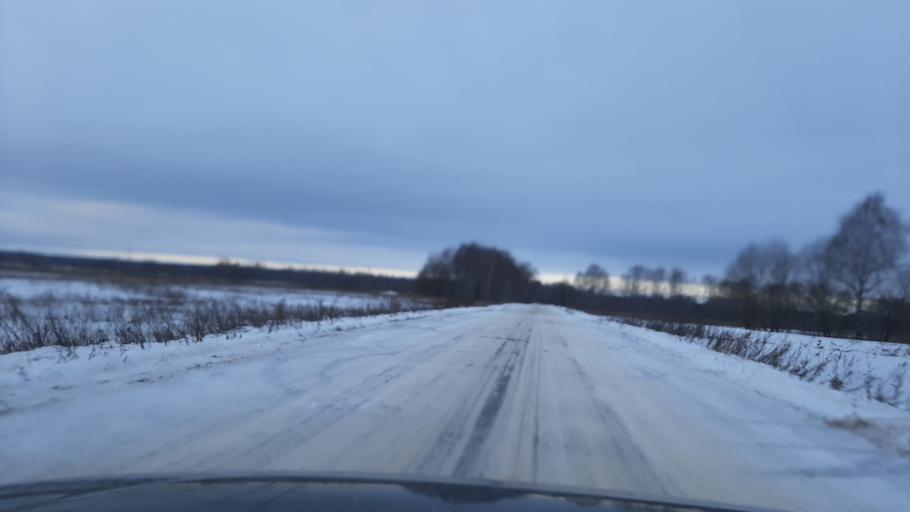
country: RU
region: Kostroma
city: Volgorechensk
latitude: 57.4367
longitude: 41.0549
